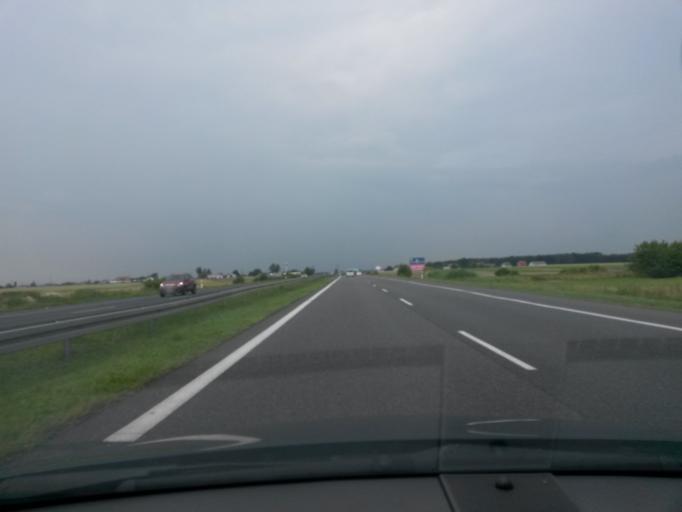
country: PL
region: Lodz Voivodeship
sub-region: Powiat piotrkowski
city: Wola Krzysztoporska
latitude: 51.3822
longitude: 19.6248
